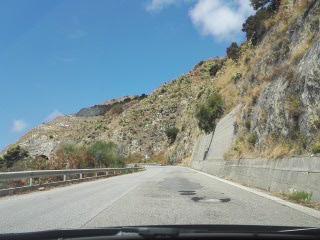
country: IT
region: Calabria
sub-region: Provincia di Vibo-Valentia
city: Joppolo
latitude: 38.5906
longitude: 15.8799
